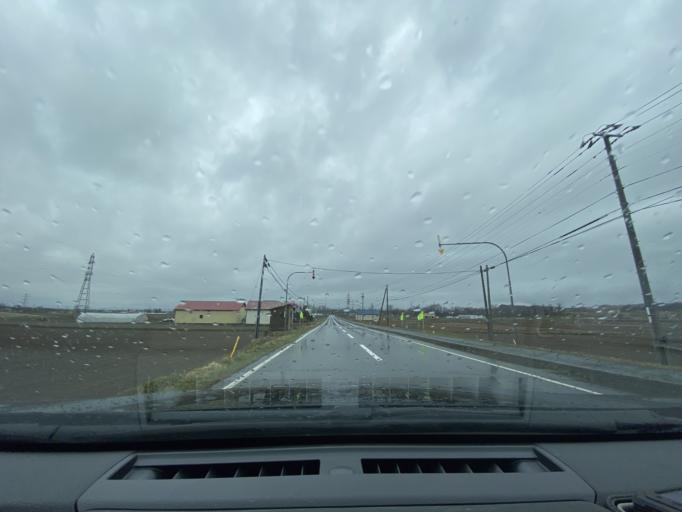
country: JP
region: Hokkaido
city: Fukagawa
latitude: 43.8130
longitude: 141.9579
